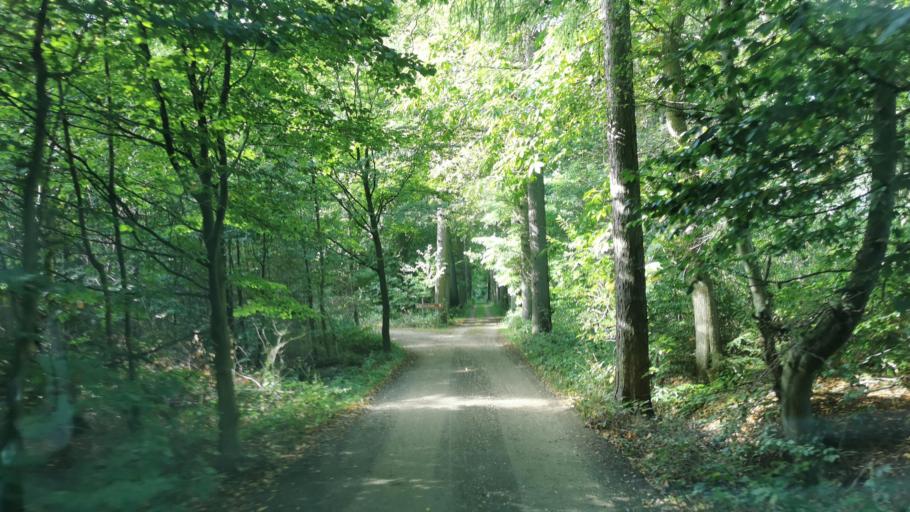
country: NL
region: Overijssel
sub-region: Gemeente Losser
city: Losser
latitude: 52.2762
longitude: 6.9610
